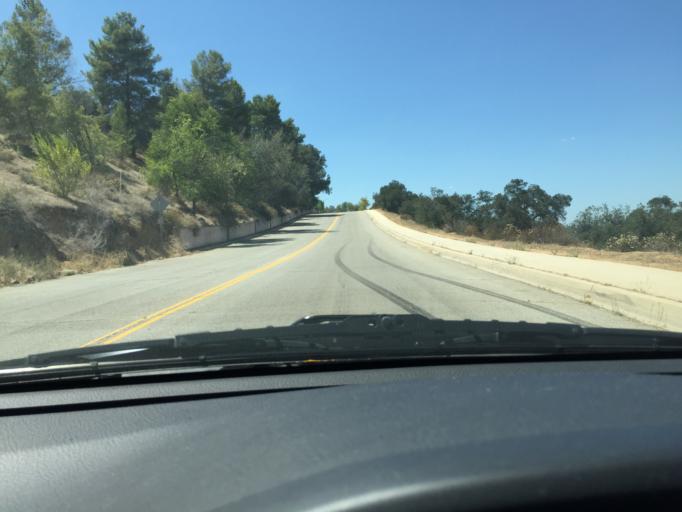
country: US
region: California
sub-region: San Bernardino County
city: Yucaipa
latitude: 34.0142
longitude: -117.0087
